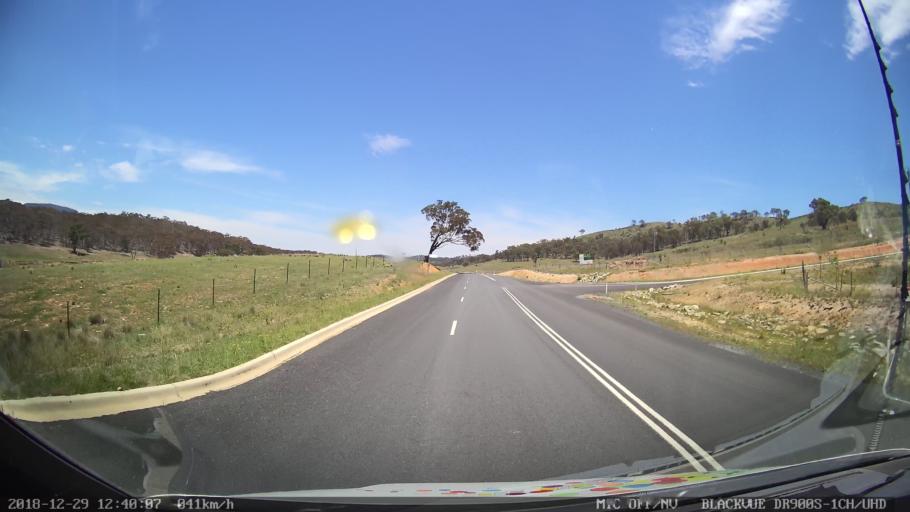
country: AU
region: Australian Capital Territory
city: Macarthur
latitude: -35.5992
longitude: 149.2260
